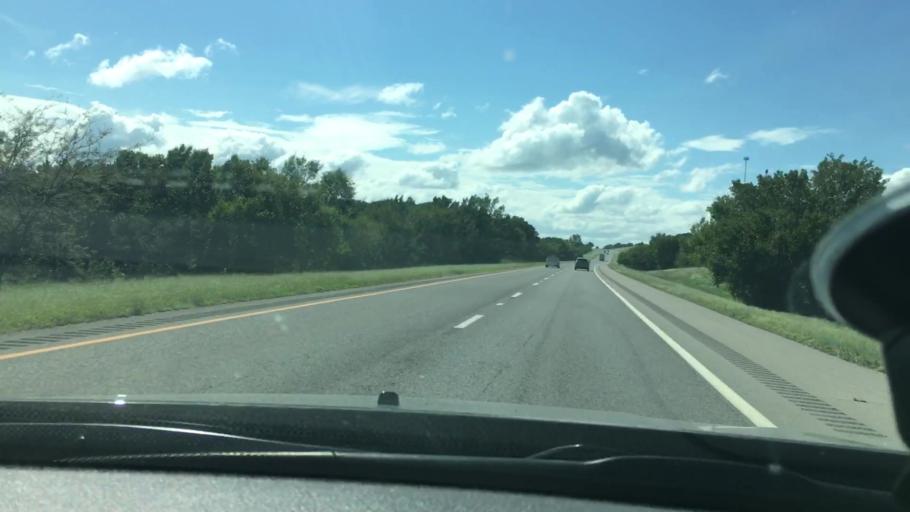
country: US
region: Oklahoma
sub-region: Muskogee County
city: Warner
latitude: 35.4573
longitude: -95.4064
